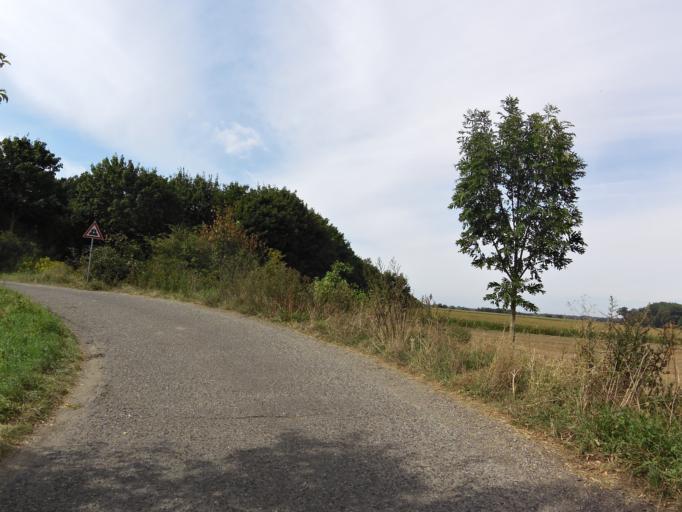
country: DE
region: Saxony
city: Schkeuditz
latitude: 51.3607
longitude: 12.2595
